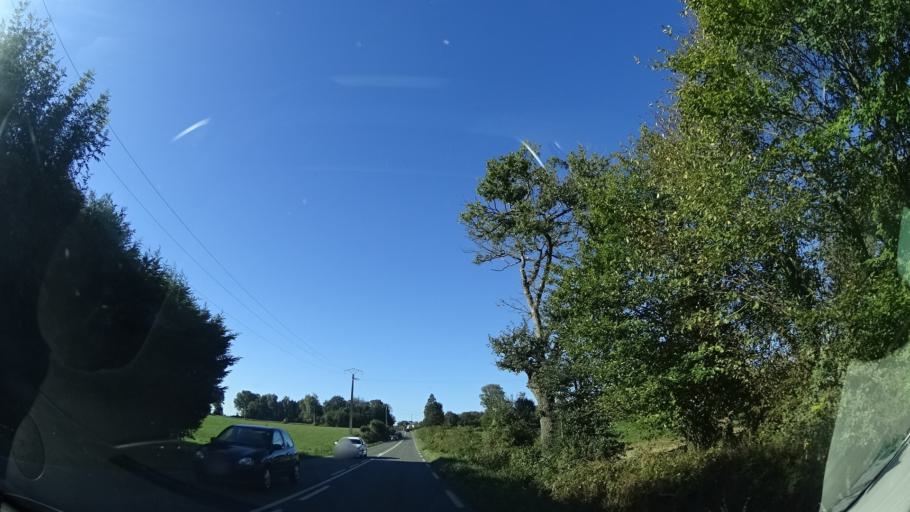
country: FR
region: Brittany
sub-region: Departement d'Ille-et-Vilaine
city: La Meziere
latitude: 48.2058
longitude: -1.7474
